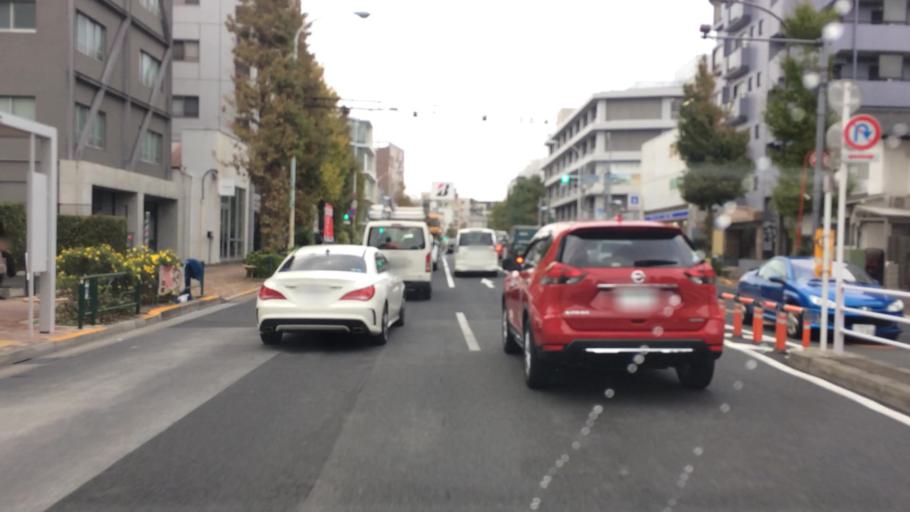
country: JP
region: Tokyo
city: Tokyo
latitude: 35.6273
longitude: 139.6925
